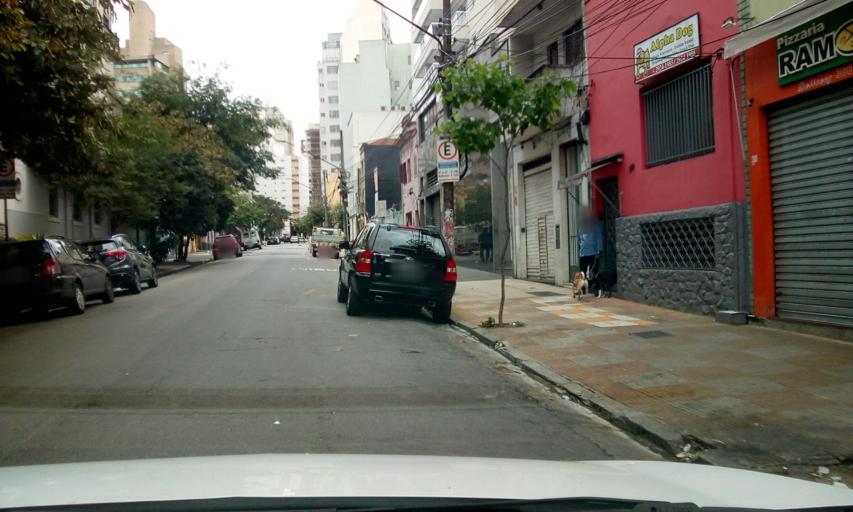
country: BR
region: Sao Paulo
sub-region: Sao Paulo
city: Sao Paulo
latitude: -23.5400
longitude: -46.6532
